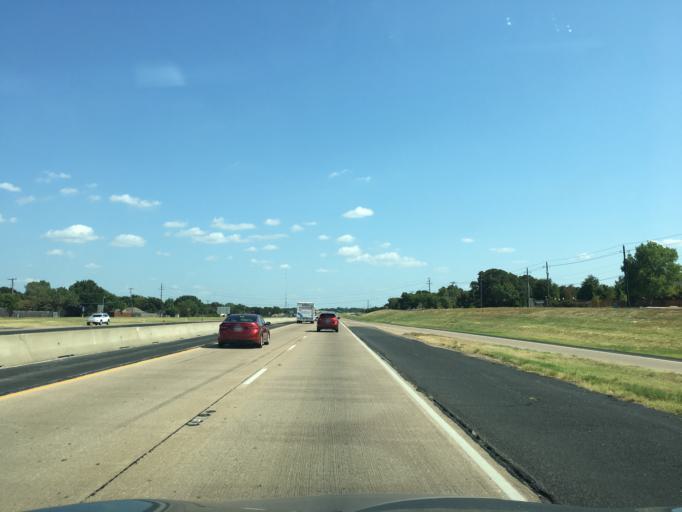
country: US
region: Texas
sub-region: Tarrant County
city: Kennedale
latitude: 32.6440
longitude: -97.1838
